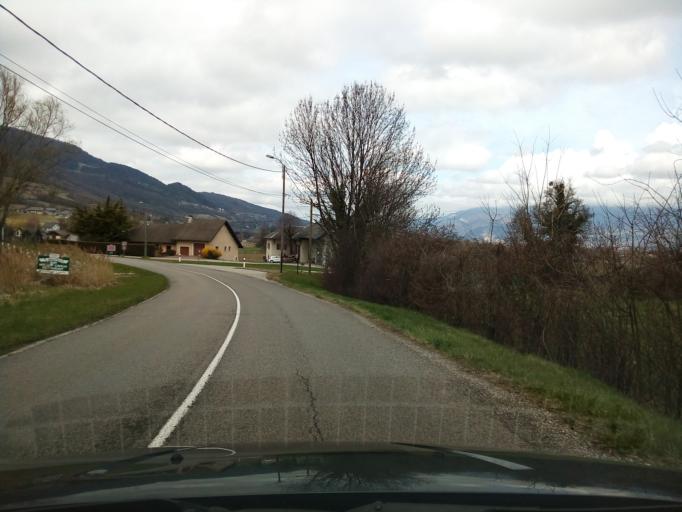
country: FR
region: Rhone-Alpes
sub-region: Departement de la Savoie
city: Saint-Baldoph
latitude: 45.5033
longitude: 5.9655
